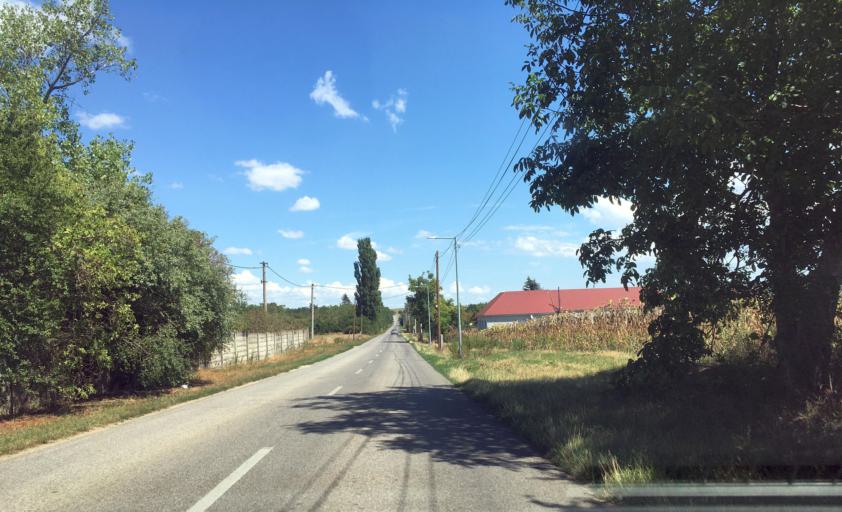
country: HU
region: Komarom-Esztergom
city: Sutto
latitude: 47.8414
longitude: 18.4288
